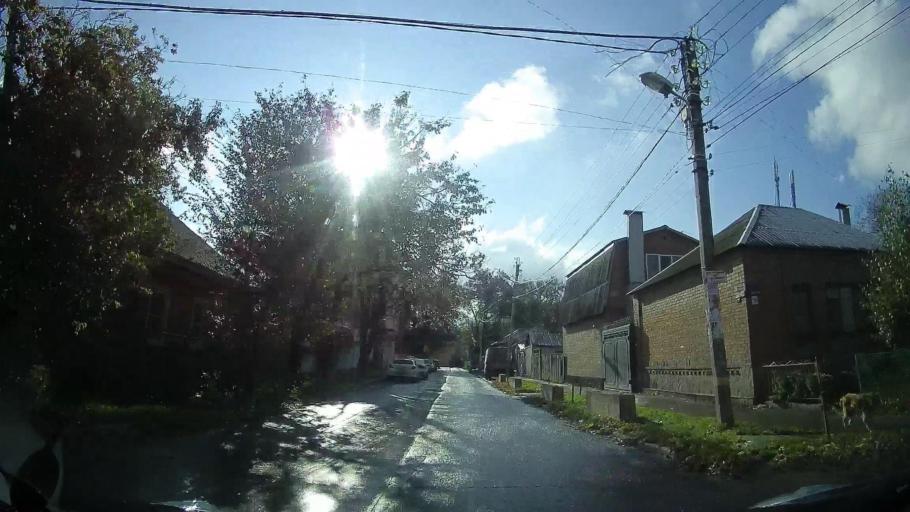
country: RU
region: Rostov
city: Severnyy
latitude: 47.2640
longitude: 39.6691
